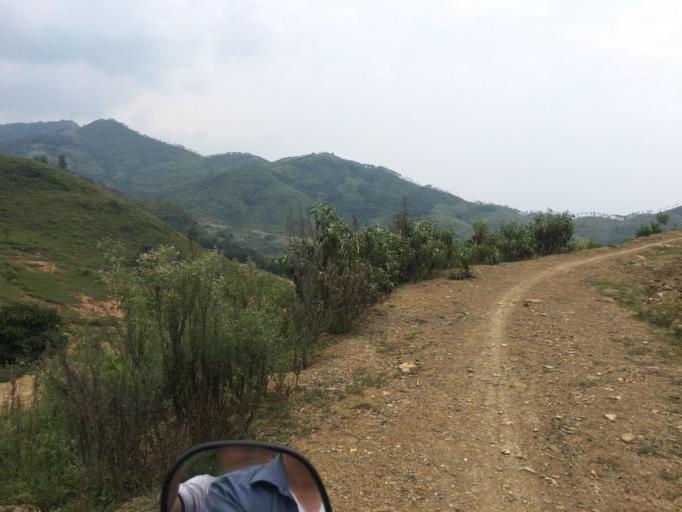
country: CN
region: Guizhou Sheng
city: Anshun
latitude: 25.4873
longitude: 105.9243
